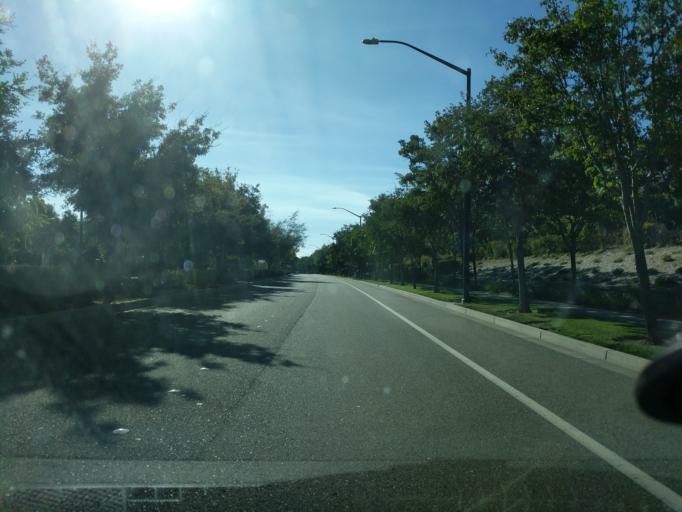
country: US
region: California
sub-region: Contra Costa County
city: Blackhawk
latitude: 37.7632
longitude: -121.8963
